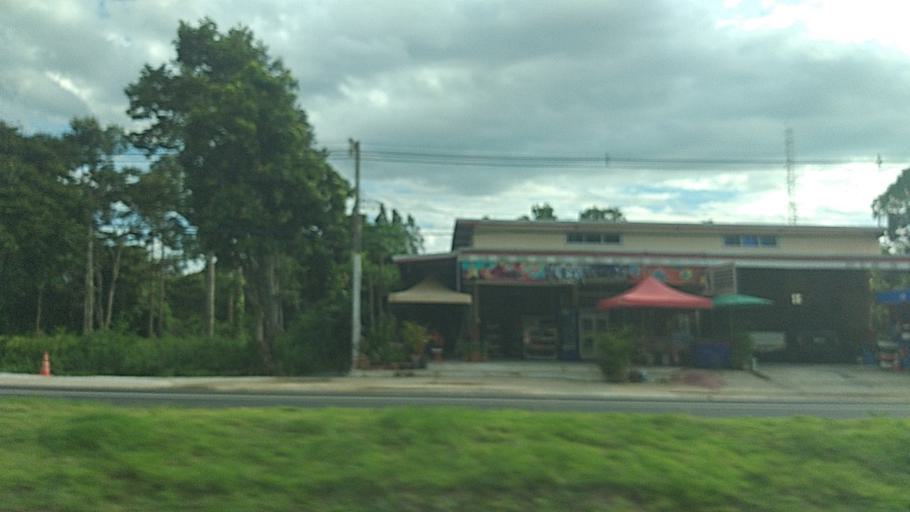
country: TH
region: Surin
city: Prasat
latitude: 14.5876
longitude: 103.4697
